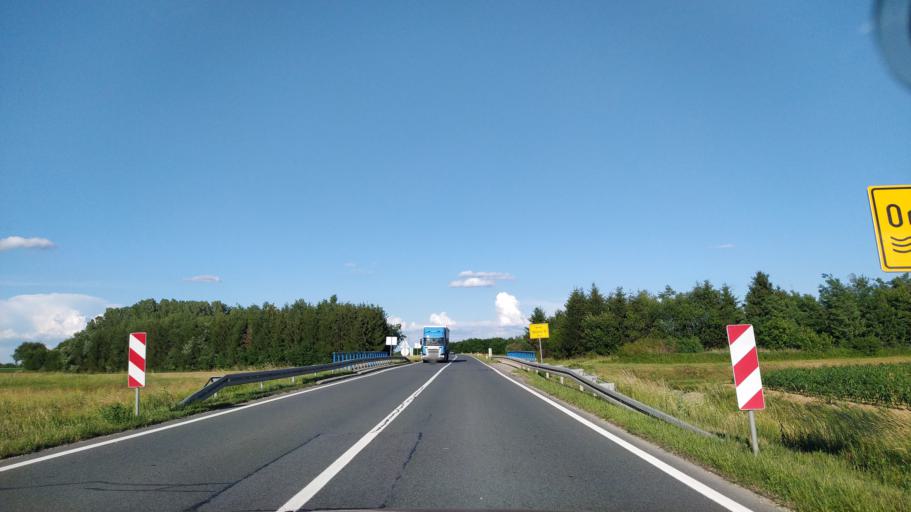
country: HR
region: Virovitick-Podravska
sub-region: Grad Virovitica
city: Virovitica
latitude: 45.8488
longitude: 17.3713
